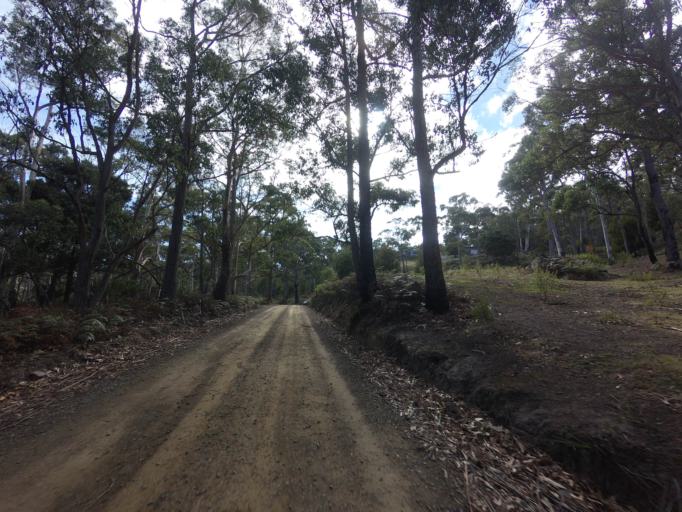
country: AU
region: Tasmania
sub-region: Clarence
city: Sandford
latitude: -43.0756
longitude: 147.6679
